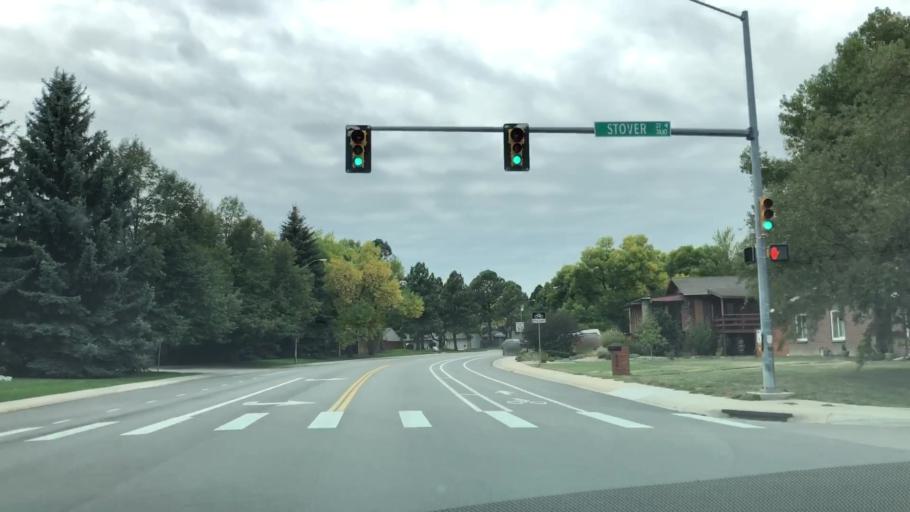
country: US
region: Colorado
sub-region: Larimer County
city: Fort Collins
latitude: 40.5461
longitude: -105.0660
